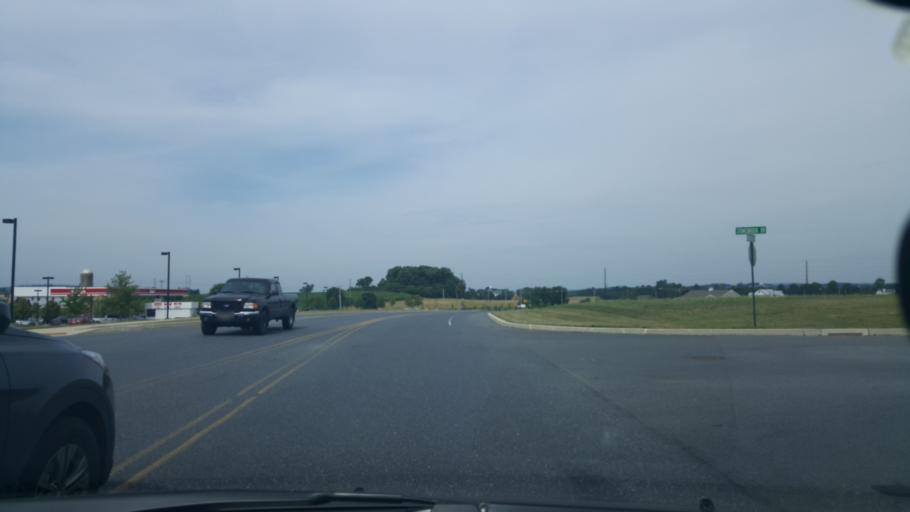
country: US
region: Pennsylvania
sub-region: Lebanon County
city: Campbelltown
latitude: 40.2843
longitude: -76.5892
